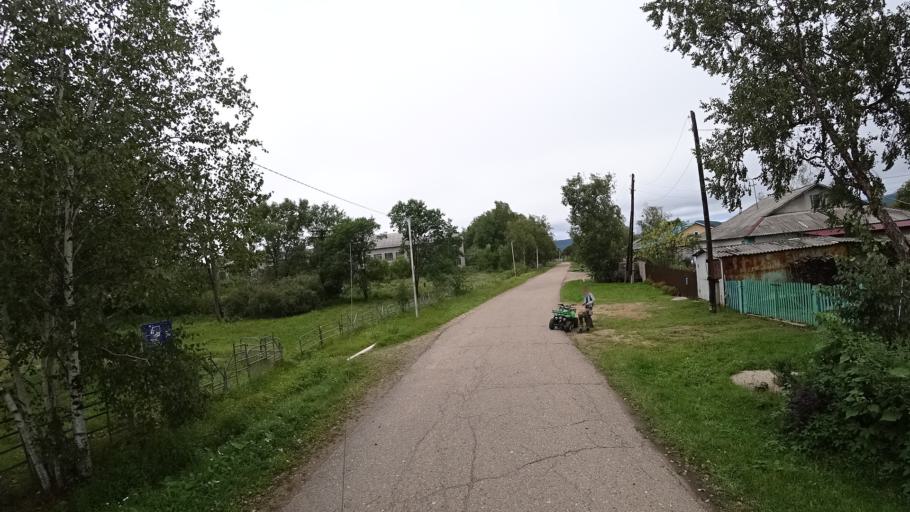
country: RU
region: Primorskiy
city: Monastyrishche
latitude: 44.0819
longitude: 132.5822
